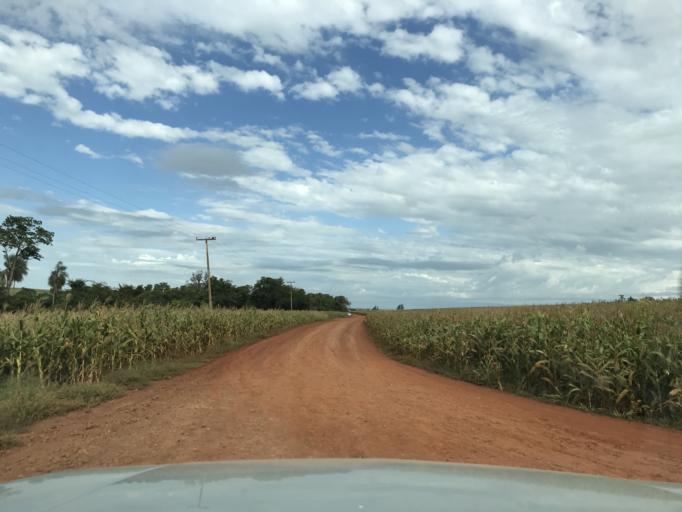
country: BR
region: Parana
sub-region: Palotina
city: Palotina
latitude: -24.3091
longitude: -53.8084
